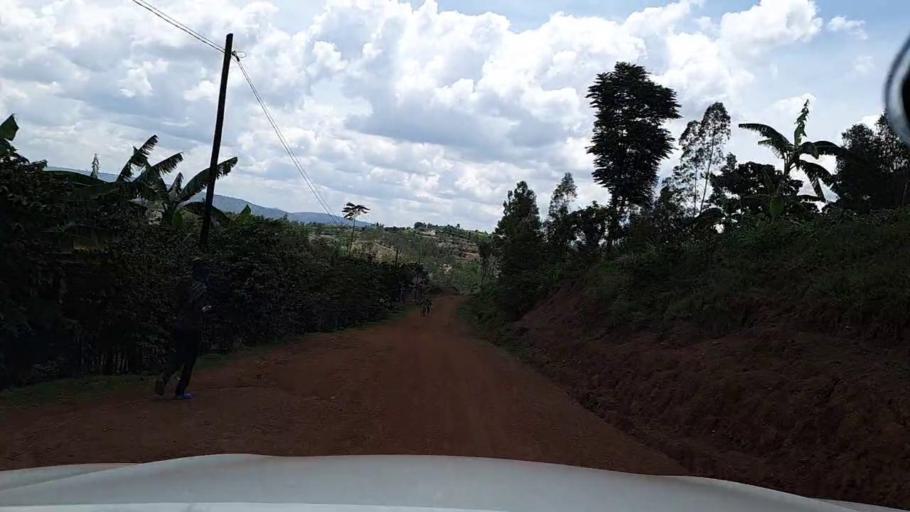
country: RW
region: Southern Province
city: Butare
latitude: -2.7587
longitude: 29.7474
